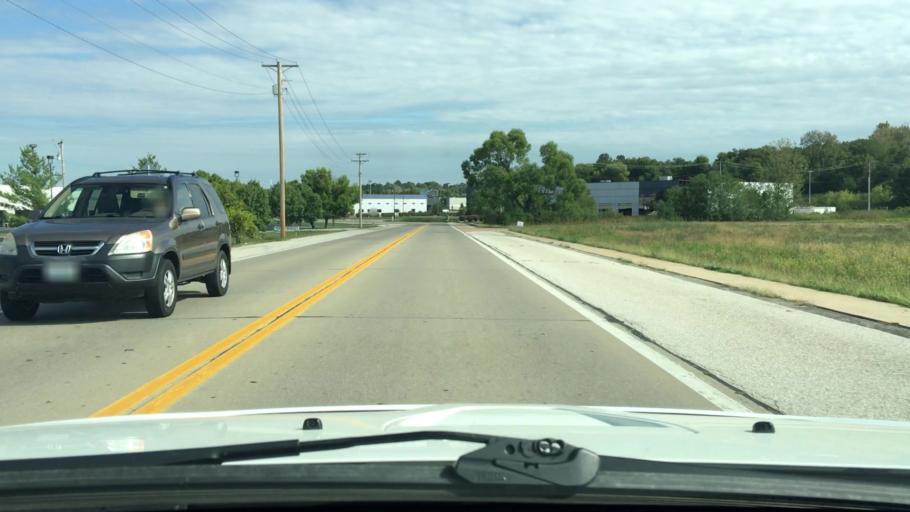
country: US
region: Missouri
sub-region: Saint Charles County
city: Saint Charles
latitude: 38.8202
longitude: -90.5107
